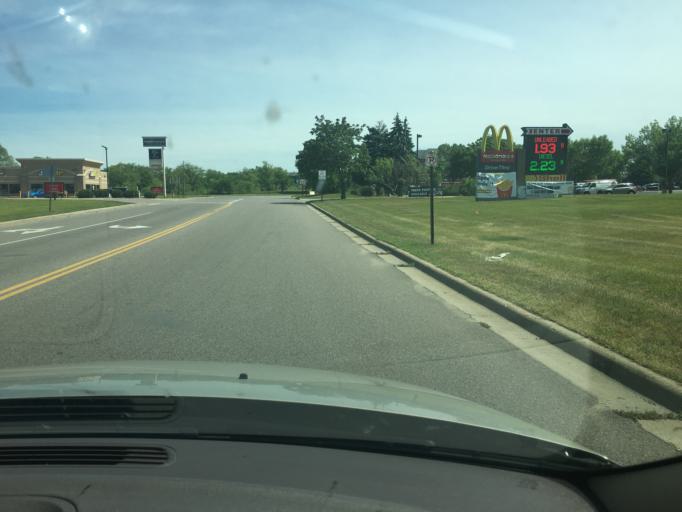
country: US
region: Minnesota
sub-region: Stearns County
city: Saint Augusta
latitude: 45.4953
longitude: -94.1496
